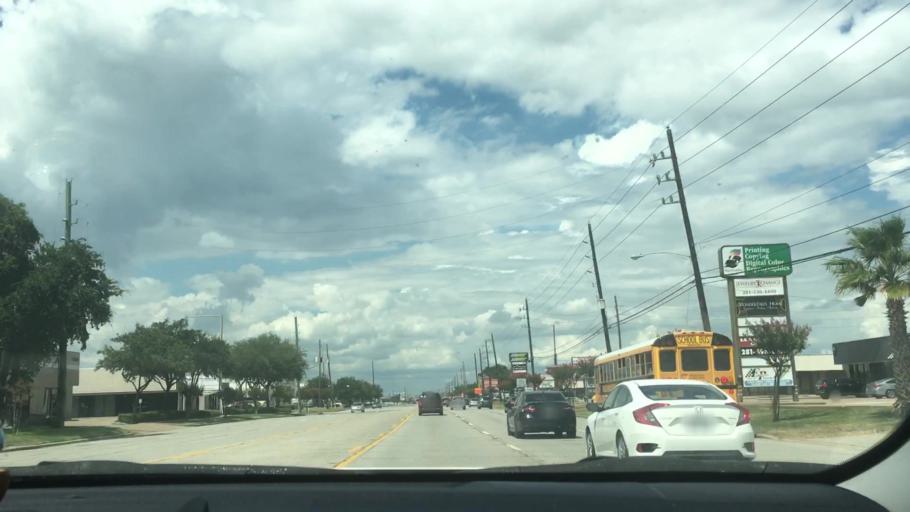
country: US
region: Texas
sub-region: Fort Bend County
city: Stafford
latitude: 29.6335
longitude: -95.5650
